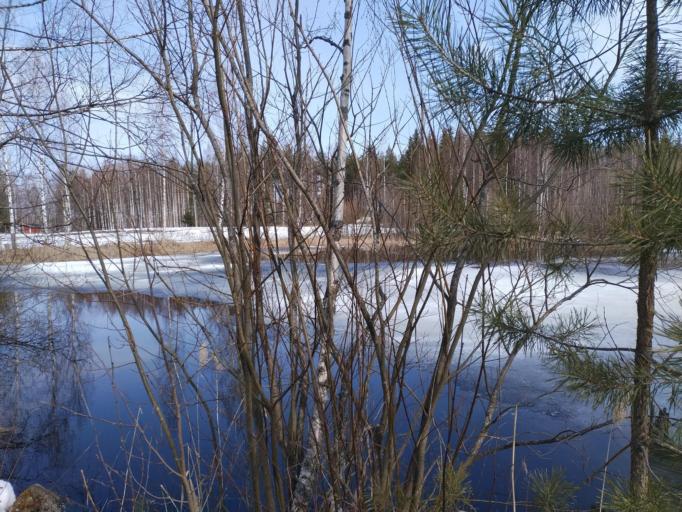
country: FI
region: Southern Savonia
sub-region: Savonlinna
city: Punkaharju
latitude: 61.6708
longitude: 29.2909
